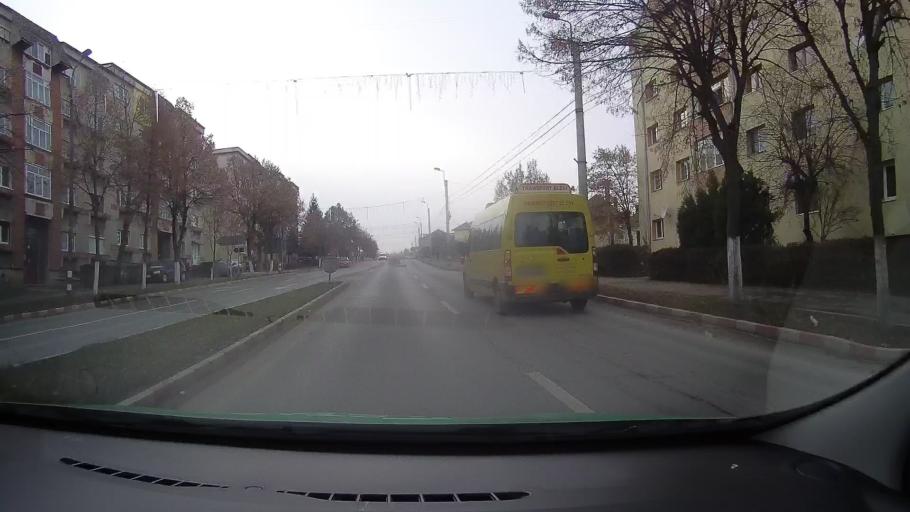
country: RO
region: Hunedoara
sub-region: Municipiul Orastie
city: Orastie
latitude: 45.8416
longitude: 23.1956
